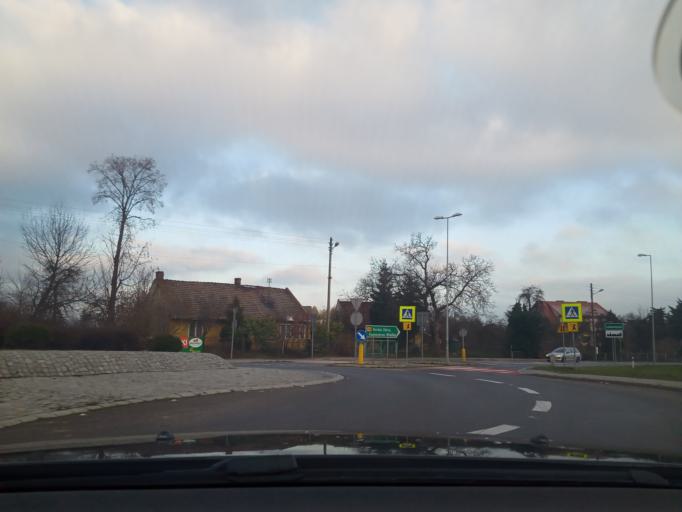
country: PL
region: Lesser Poland Voivodeship
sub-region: Powiat krakowski
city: Slomniki
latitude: 50.1366
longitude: 20.1150
